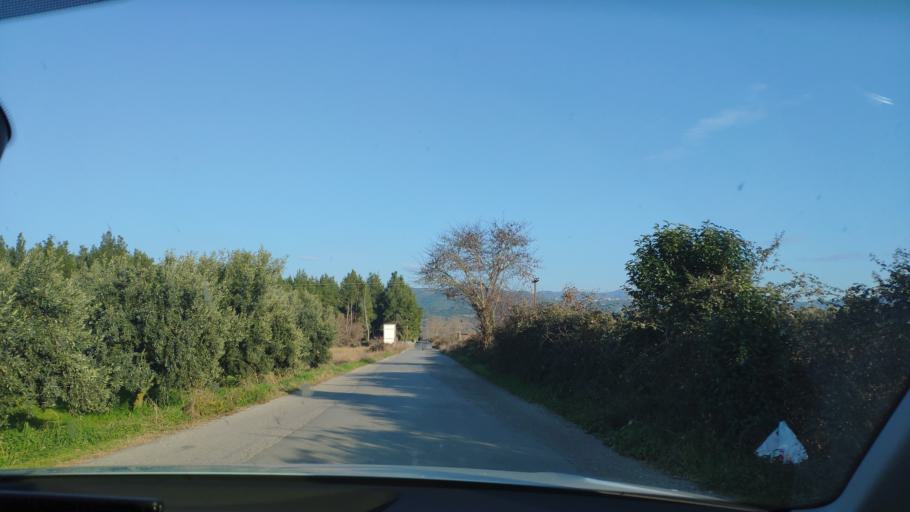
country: GR
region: West Greece
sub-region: Nomos Aitolias kai Akarnanias
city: Krikellos
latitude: 38.9307
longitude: 21.1680
